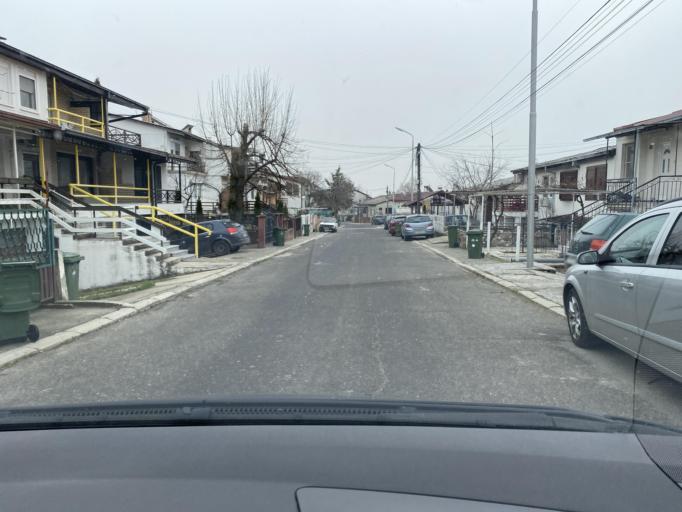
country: MK
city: Radishani
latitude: 42.0578
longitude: 21.4478
